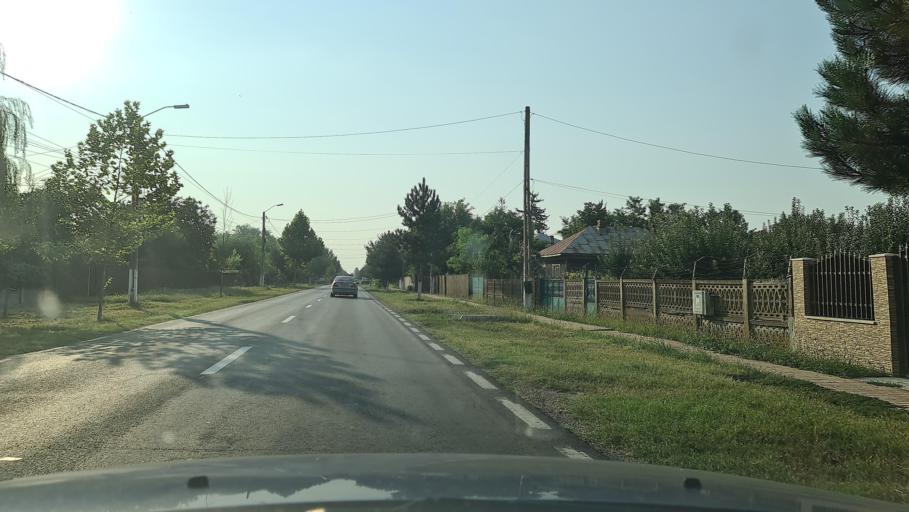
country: RO
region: Calarasi
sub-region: Comuna Dor Marunt
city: Dor Marunt
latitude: 44.4421
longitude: 26.9362
